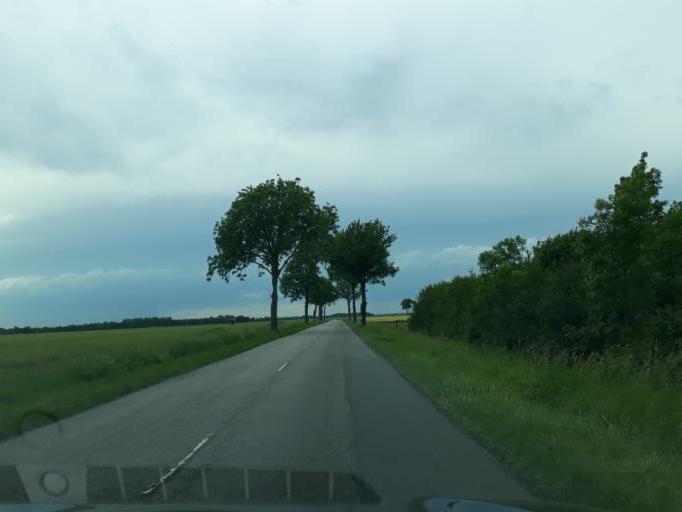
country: FR
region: Centre
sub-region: Departement du Loiret
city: Tigy
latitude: 47.8061
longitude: 2.1837
